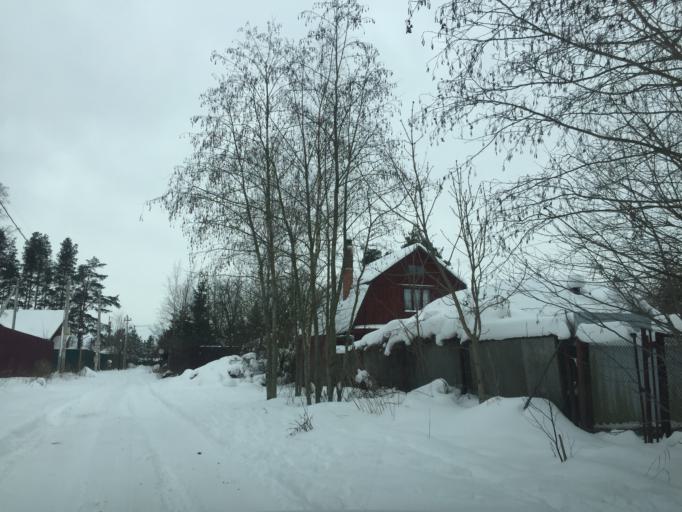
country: RU
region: Leningrad
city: Otradnoye
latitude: 59.7813
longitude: 30.7845
